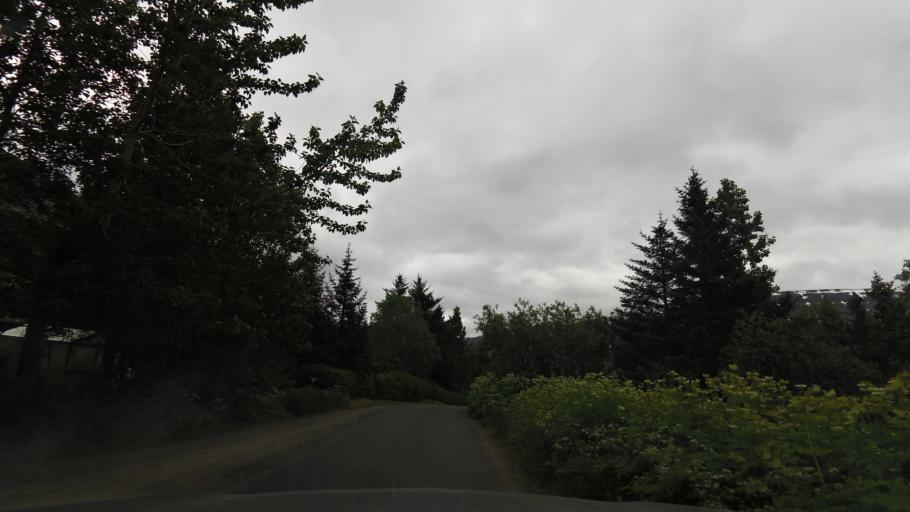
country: IS
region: Westfjords
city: Isafjoerdur
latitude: 66.0608
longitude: -23.1999
